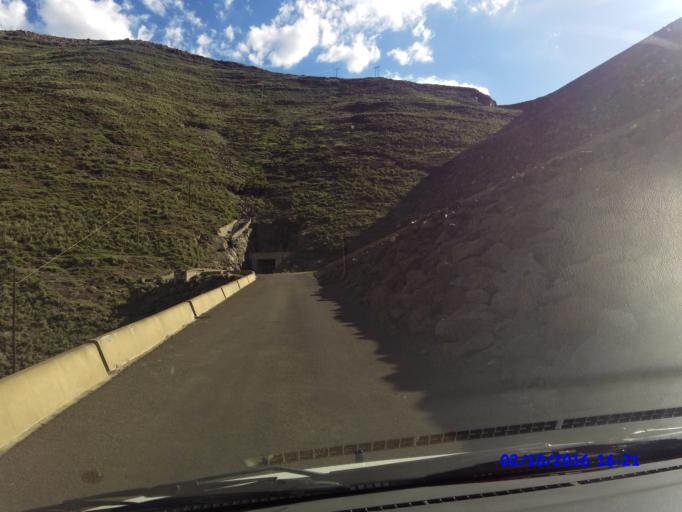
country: LS
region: Maseru
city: Nako
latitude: -29.4593
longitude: 28.0981
